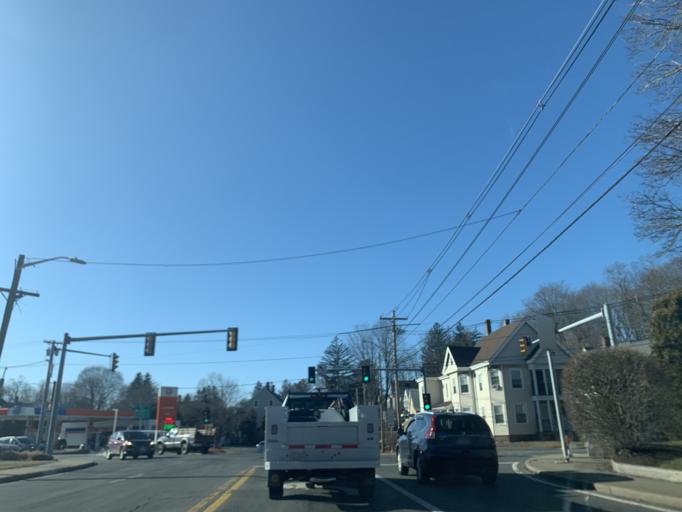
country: US
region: Massachusetts
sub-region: Middlesex County
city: Marlborough
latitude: 42.3511
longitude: -71.5405
